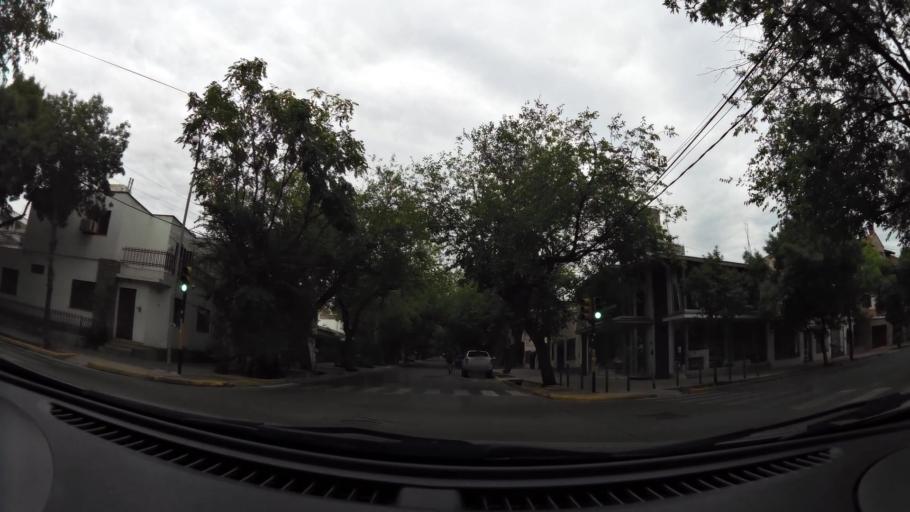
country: AR
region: Mendoza
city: Mendoza
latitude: -32.9002
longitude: -68.8468
